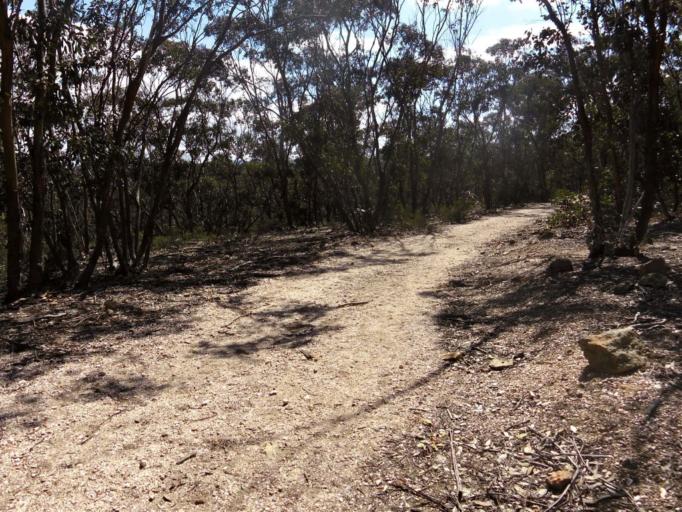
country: AU
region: Victoria
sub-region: Moorabool
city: Bacchus Marsh
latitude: -37.6636
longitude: 144.5003
